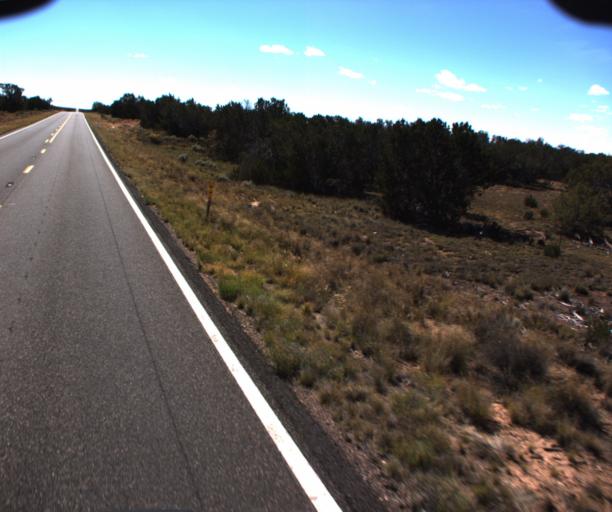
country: US
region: Arizona
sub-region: Apache County
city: Houck
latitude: 34.8860
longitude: -109.2380
